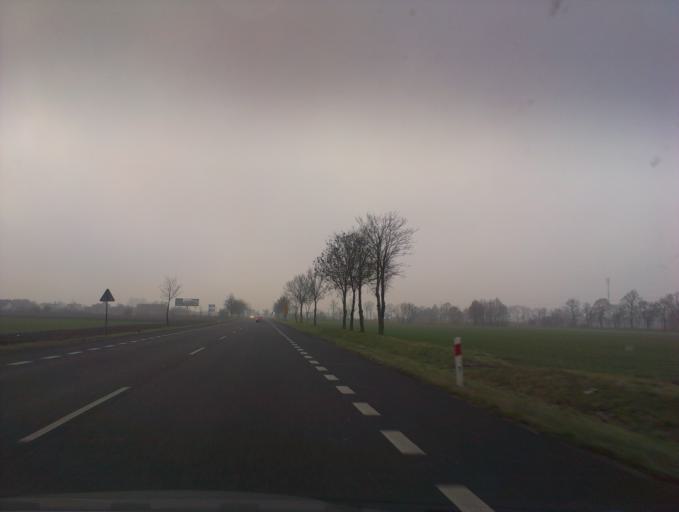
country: PL
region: Greater Poland Voivodeship
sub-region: Powiat chodzieski
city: Budzyn
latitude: 52.8956
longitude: 16.9697
